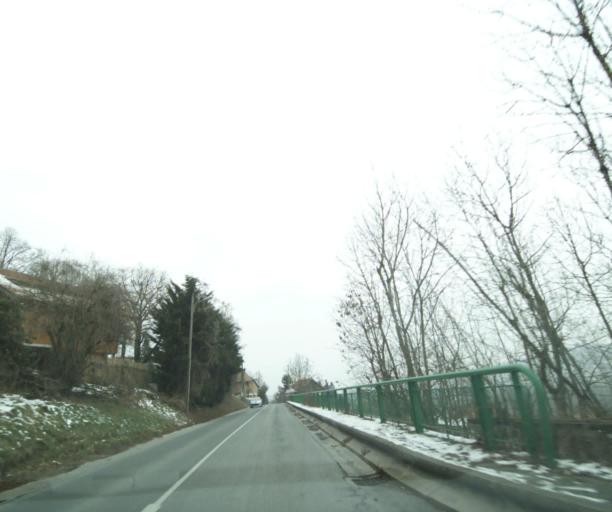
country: FR
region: Rhone-Alpes
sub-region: Departement de la Haute-Savoie
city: Vetraz-Monthoux
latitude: 46.1699
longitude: 6.2387
